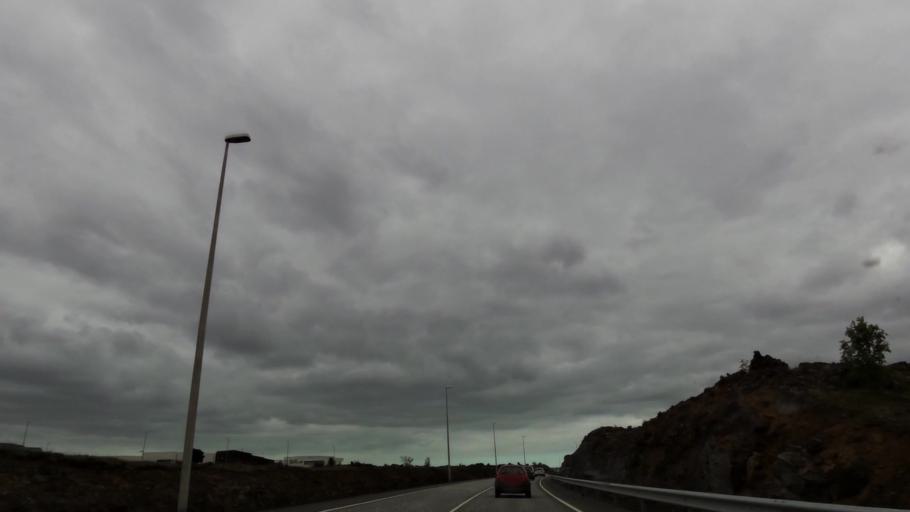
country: IS
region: Capital Region
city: Hafnarfjoerdur
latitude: 64.0864
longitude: -21.9581
